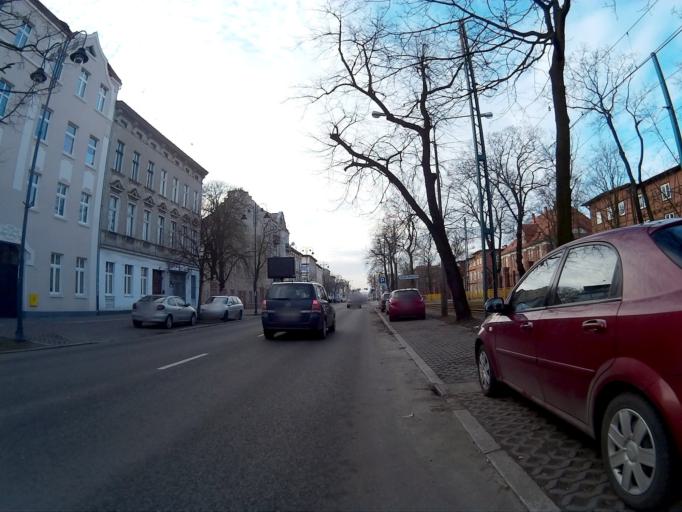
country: PL
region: Kujawsko-Pomorskie
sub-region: Bydgoszcz
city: Bydgoszcz
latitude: 53.1391
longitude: 18.0171
